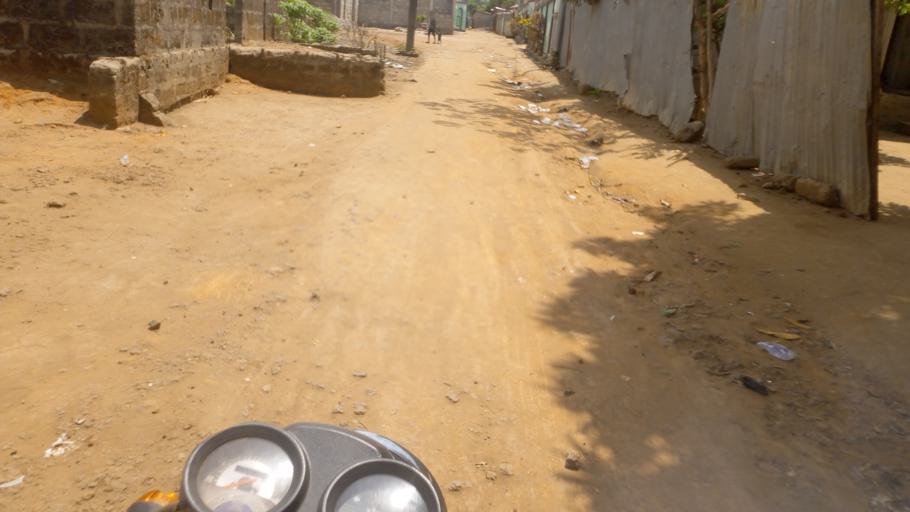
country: SL
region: Western Area
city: Waterloo
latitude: 8.3231
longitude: -13.0732
